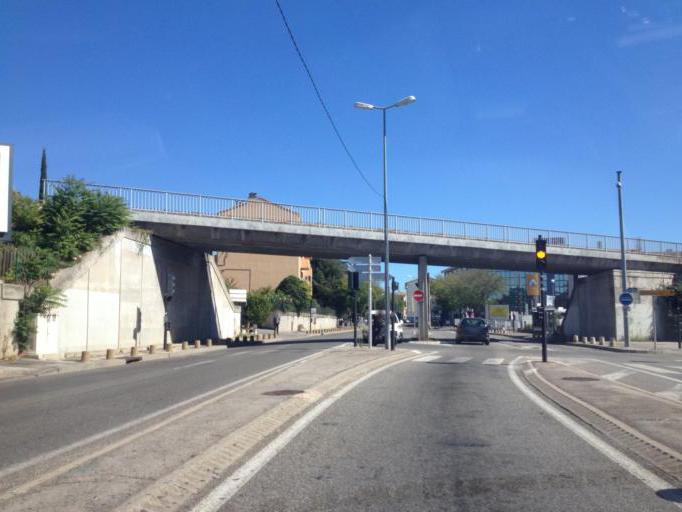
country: FR
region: Provence-Alpes-Cote d'Azur
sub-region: Departement des Bouches-du-Rhone
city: Aix-en-Provence
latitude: 43.5283
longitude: 5.4326
